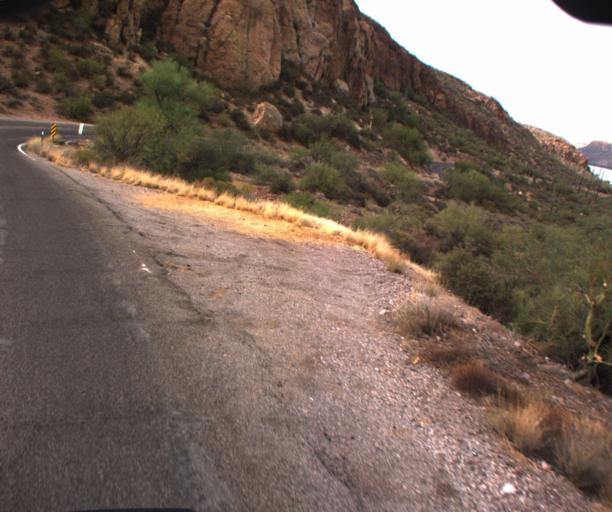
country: US
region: Arizona
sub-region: Pinal County
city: Apache Junction
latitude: 33.5294
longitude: -111.4114
